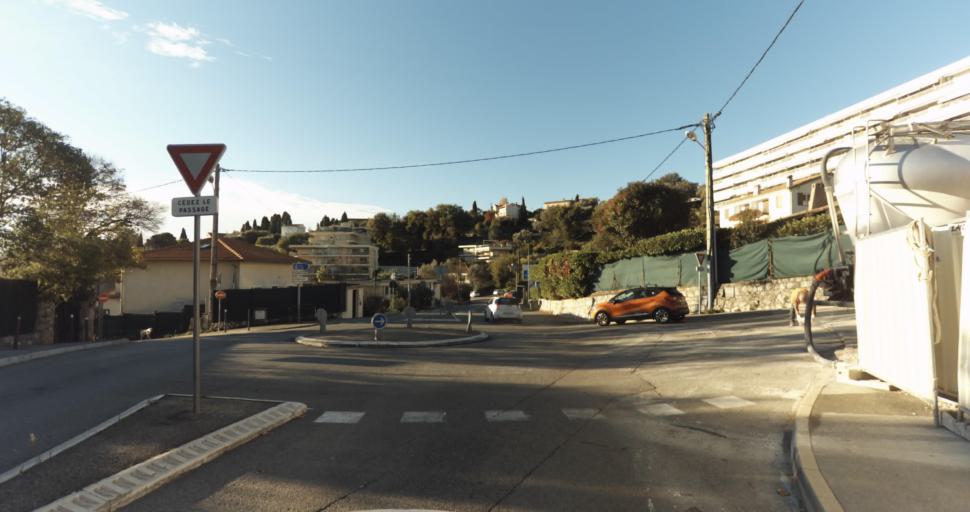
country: FR
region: Provence-Alpes-Cote d'Azur
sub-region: Departement des Alpes-Maritimes
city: Vence
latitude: 43.7213
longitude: 7.1221
